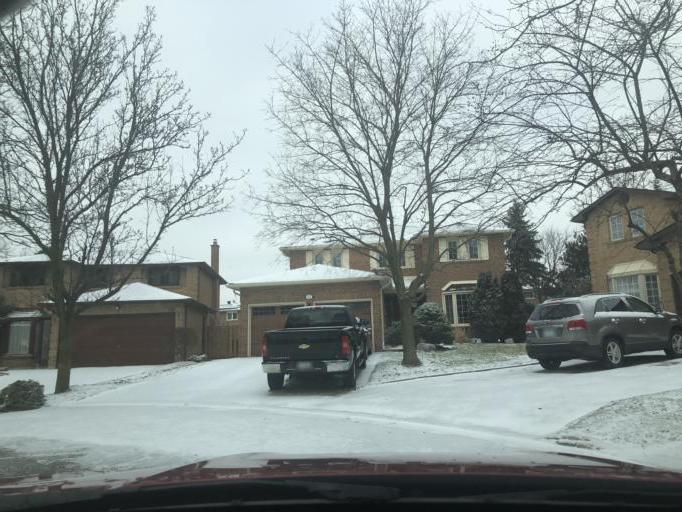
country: CA
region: Ontario
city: Markham
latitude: 43.8706
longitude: -79.2409
